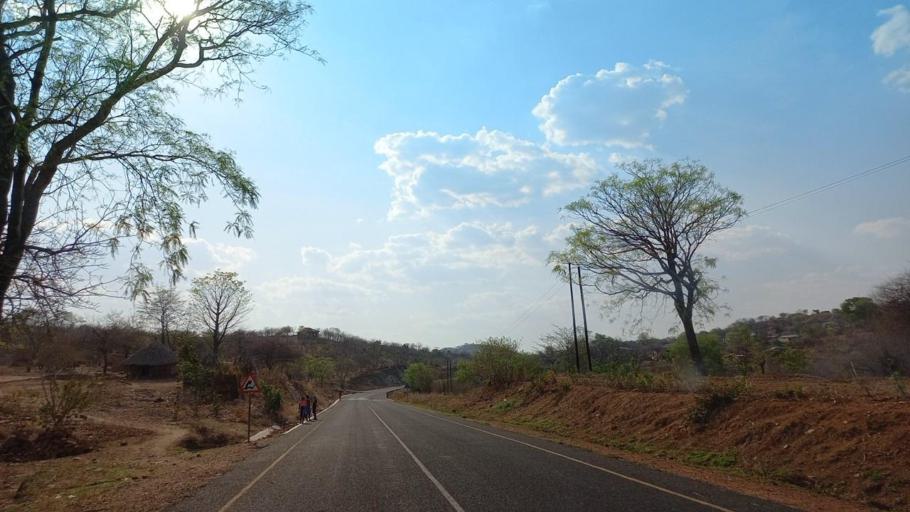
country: ZM
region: Lusaka
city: Luangwa
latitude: -14.9884
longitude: 30.2101
